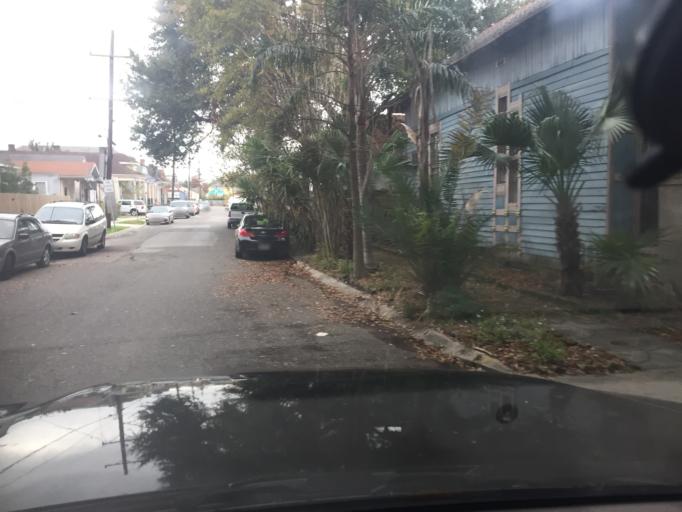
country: US
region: Louisiana
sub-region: Orleans Parish
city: New Orleans
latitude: 29.9737
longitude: -90.0780
